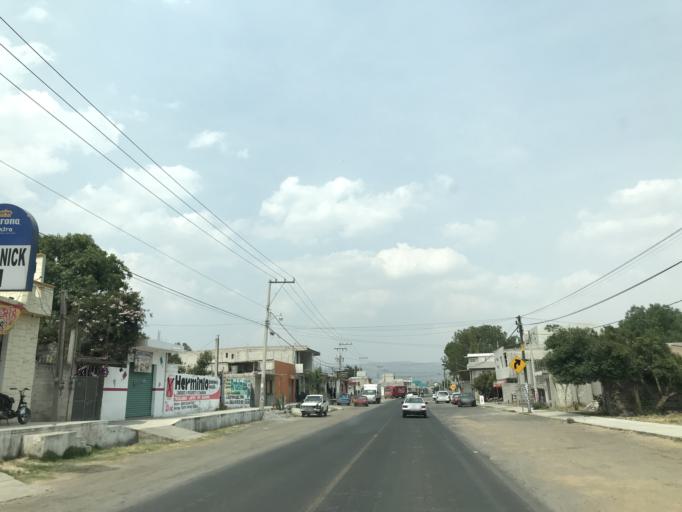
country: MX
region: Tlaxcala
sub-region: Ixtacuixtla de Mariano Matamoros
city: Santa Justina Ecatepec
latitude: 19.3095
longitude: -98.3519
